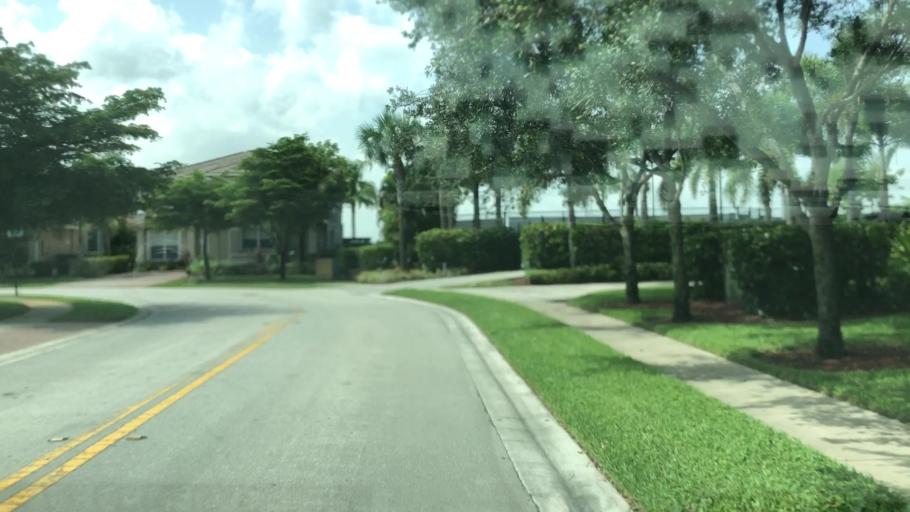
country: US
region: Florida
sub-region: Miami-Dade County
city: Palm Springs North
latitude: 25.9650
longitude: -80.3792
